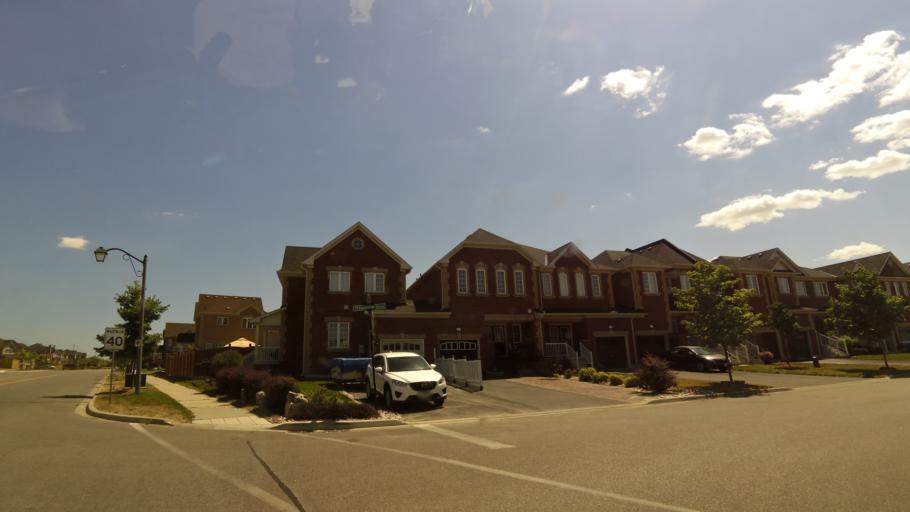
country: CA
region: Ontario
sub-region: Halton
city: Milton
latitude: 43.6332
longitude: -79.8734
